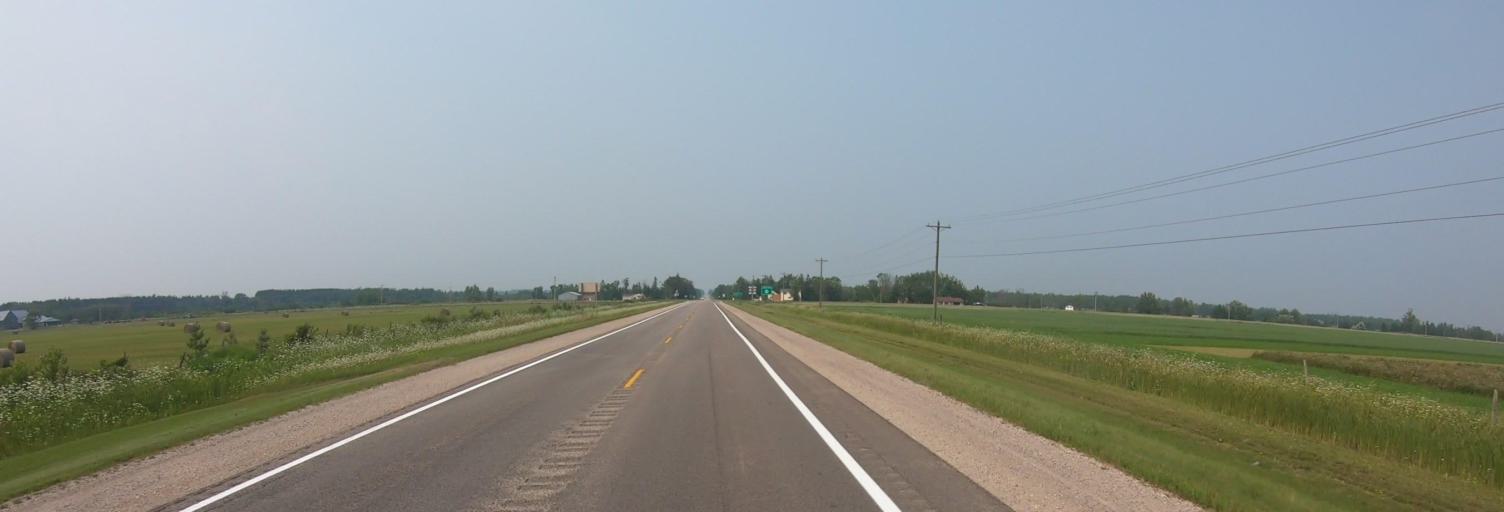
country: US
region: Michigan
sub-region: Chippewa County
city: Sault Ste. Marie
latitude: 46.1836
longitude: -84.3635
